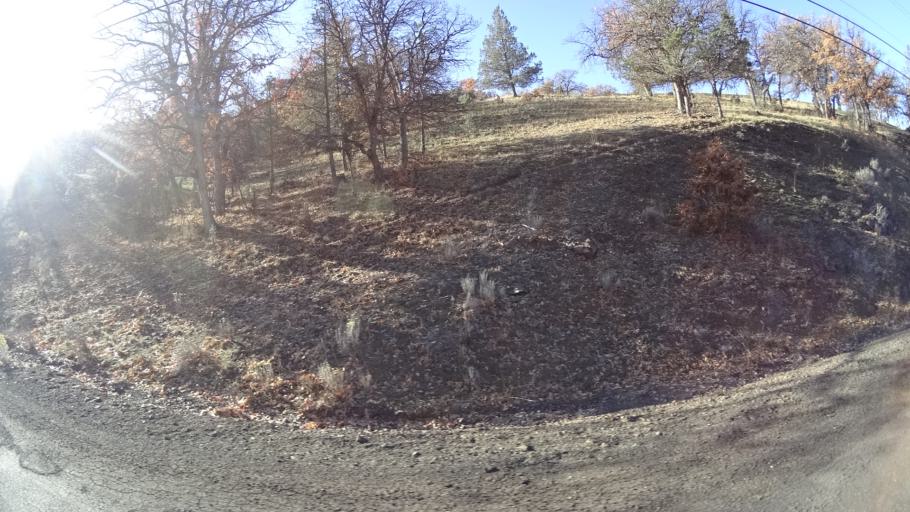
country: US
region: California
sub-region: Siskiyou County
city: Montague
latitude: 41.9162
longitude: -122.4459
